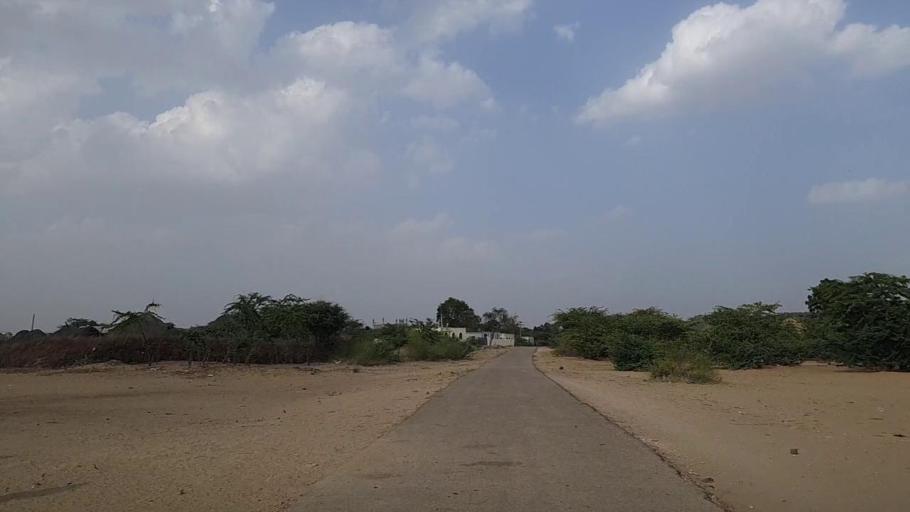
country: PK
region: Sindh
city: Islamkot
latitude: 24.7971
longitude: 70.2050
